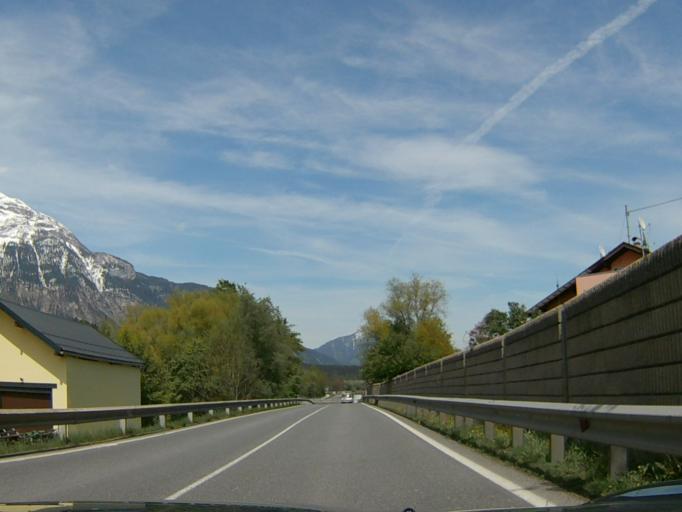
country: AT
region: Tyrol
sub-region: Politischer Bezirk Schwaz
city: Wiesing
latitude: 47.3901
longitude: 11.7949
